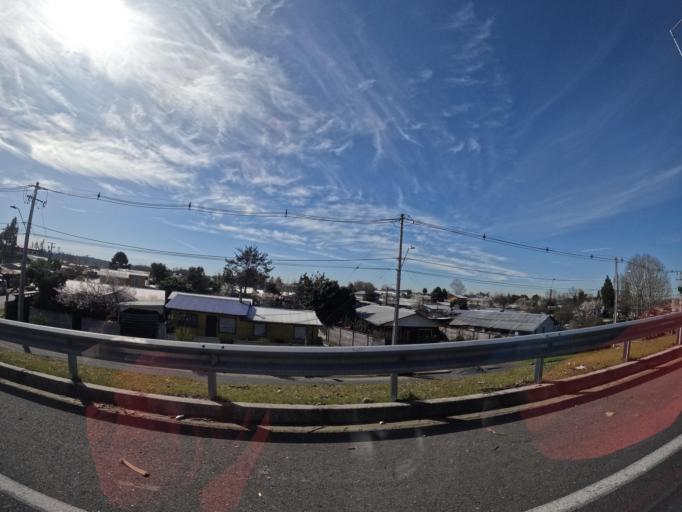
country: CL
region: Biobio
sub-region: Provincia de Biobio
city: Cabrero
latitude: -37.0401
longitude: -72.4033
